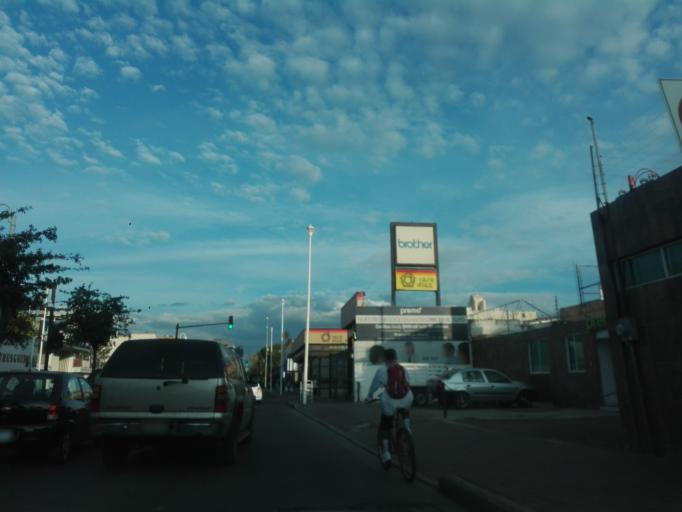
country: MX
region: Guanajuato
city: Leon
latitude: 21.1174
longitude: -101.6660
